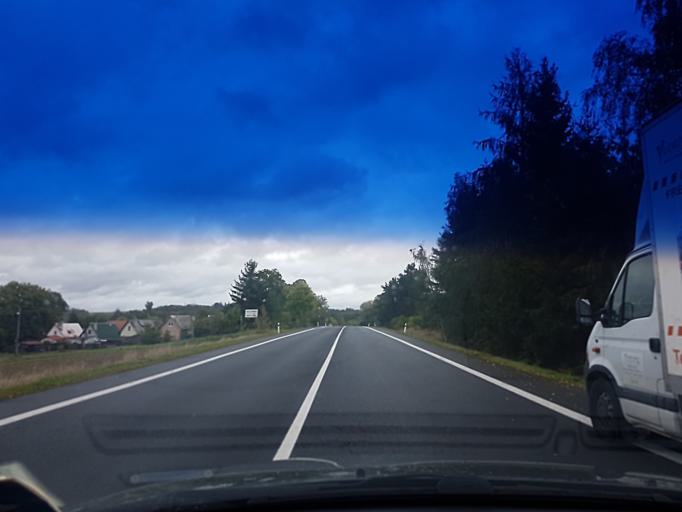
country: CZ
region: Karlovarsky
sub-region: Okres Cheb
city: Frantiskovy Lazne
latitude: 50.0815
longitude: 12.3240
